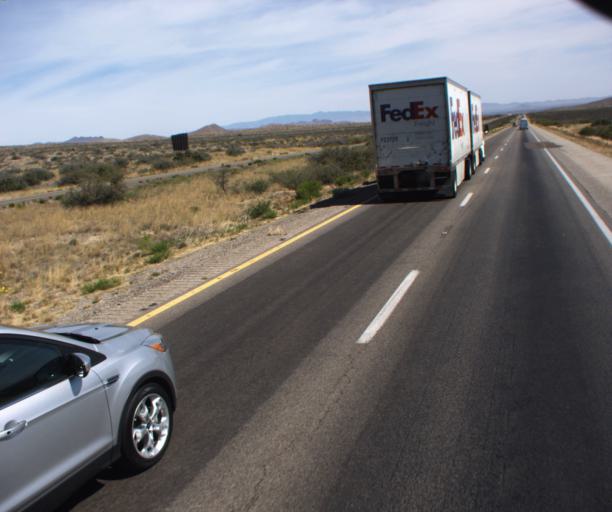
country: US
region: Arizona
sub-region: Cochise County
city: Willcox
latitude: 32.1163
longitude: -110.0196
